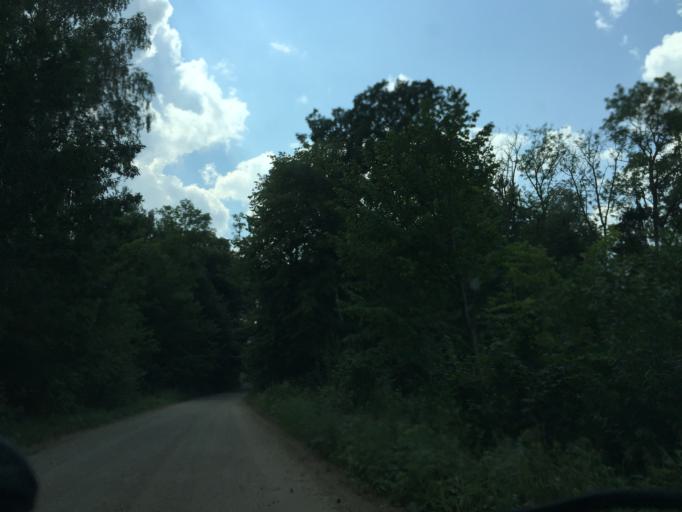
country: LT
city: Zagare
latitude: 56.3745
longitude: 23.1674
